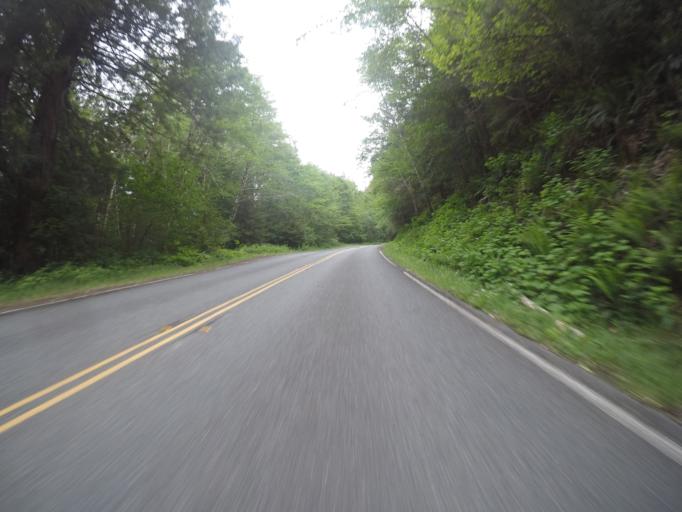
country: US
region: California
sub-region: Del Norte County
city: Bertsch-Oceanview
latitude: 41.7686
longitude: -124.0109
